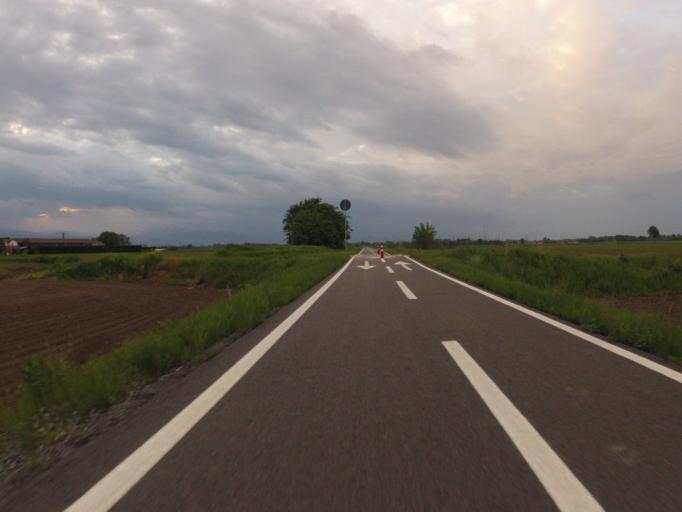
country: IT
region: Piedmont
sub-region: Provincia di Torino
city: Villafranca Piemonte
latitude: 44.7949
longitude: 7.5067
